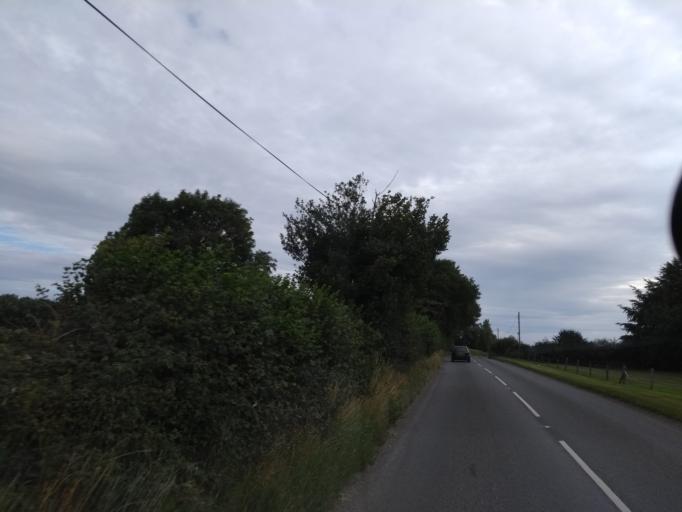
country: GB
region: England
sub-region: Somerset
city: Crewkerne
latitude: 50.8618
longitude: -2.7701
